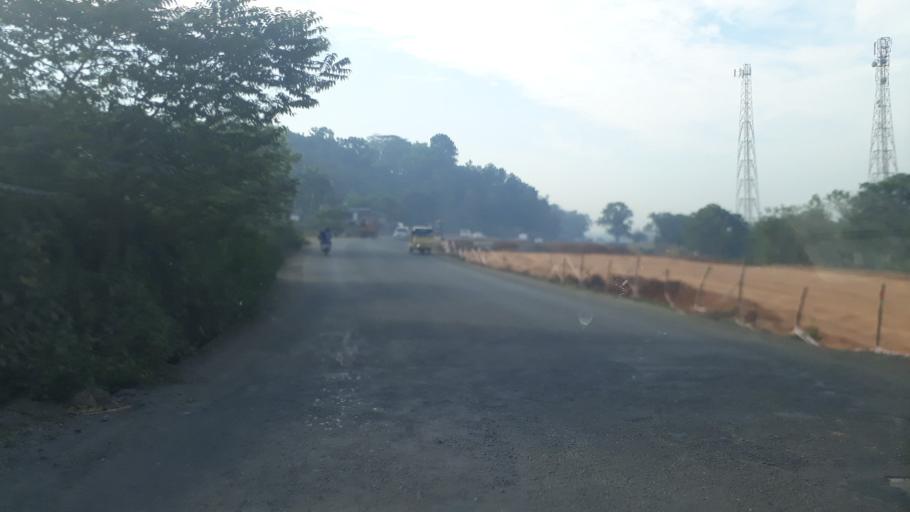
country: IN
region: Maharashtra
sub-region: Raigarh
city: Pen
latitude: 18.8561
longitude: 73.0989
